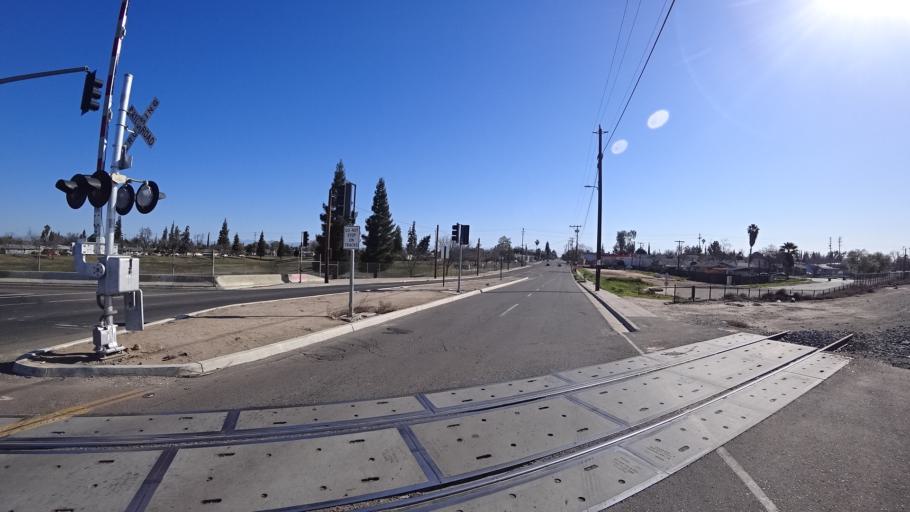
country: US
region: California
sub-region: Fresno County
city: West Park
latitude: 36.7647
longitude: -119.8291
